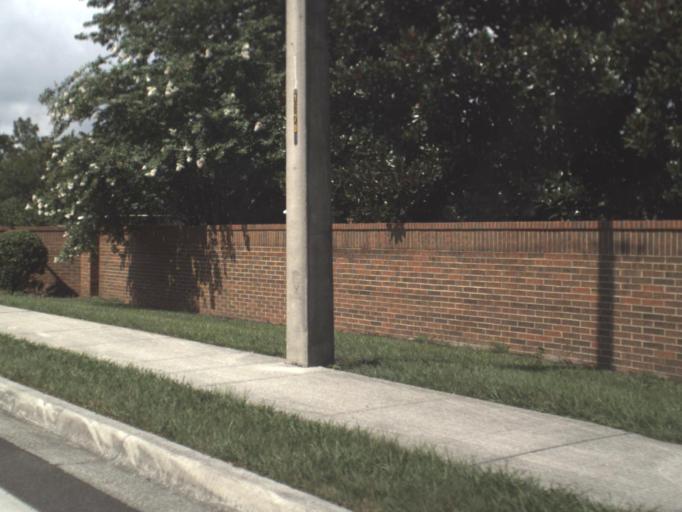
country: US
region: Florida
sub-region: Saint Johns County
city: Fruit Cove
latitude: 30.0939
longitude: -81.6280
